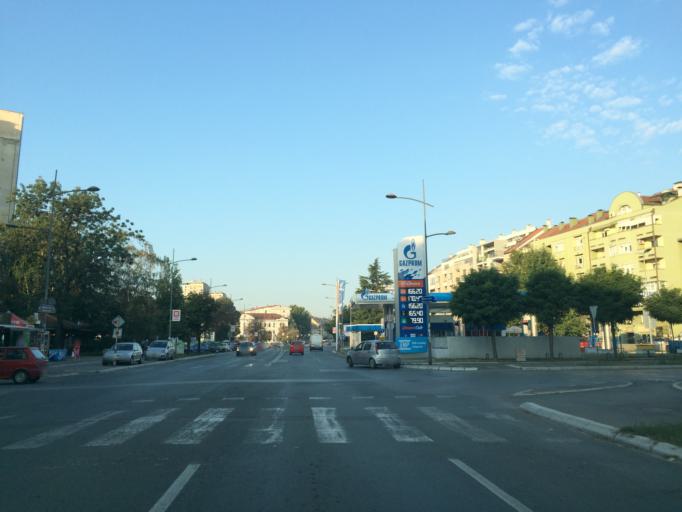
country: RS
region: Autonomna Pokrajina Vojvodina
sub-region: Juznobacki Okrug
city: Novi Sad
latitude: 45.2497
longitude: 19.8456
